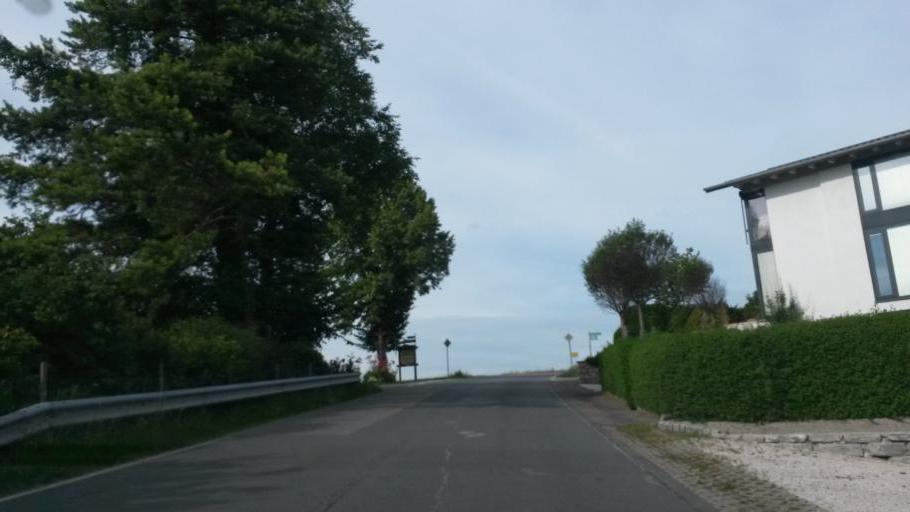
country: DE
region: Bavaria
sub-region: Upper Bavaria
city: Prien am Chiemsee
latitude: 47.8238
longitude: 12.3439
